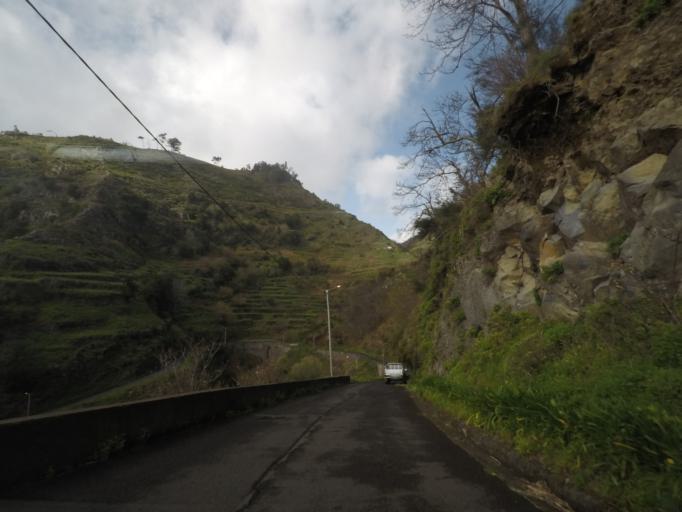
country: PT
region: Madeira
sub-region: Ribeira Brava
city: Campanario
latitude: 32.7023
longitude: -17.0248
